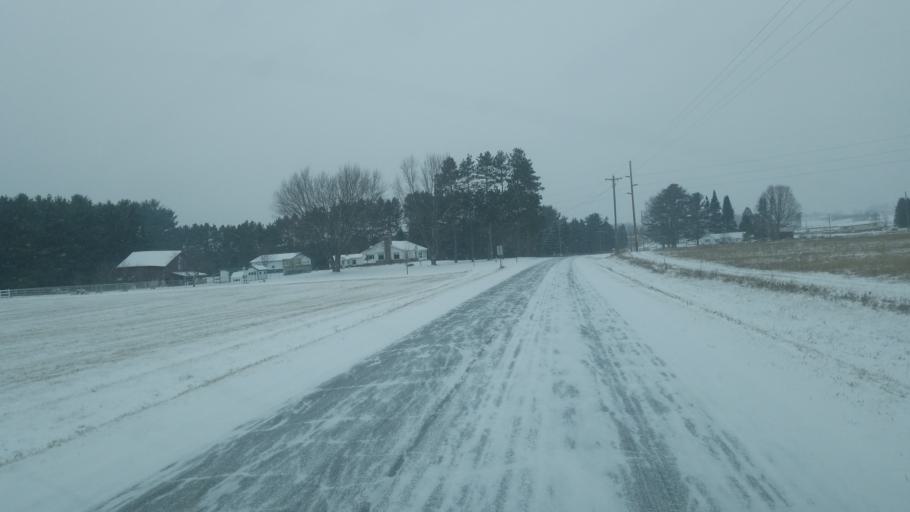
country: US
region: Michigan
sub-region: Osceola County
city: Reed City
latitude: 43.8131
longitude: -85.4037
